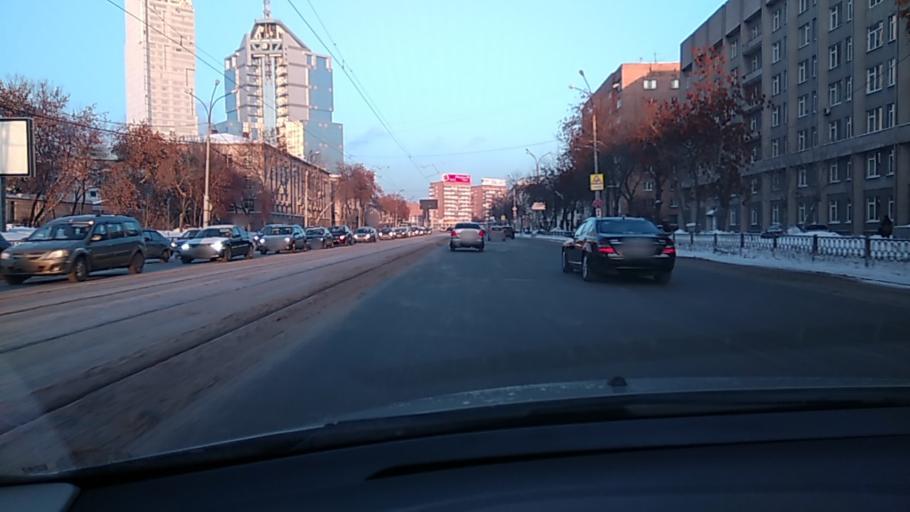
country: RU
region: Sverdlovsk
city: Yekaterinburg
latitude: 56.8531
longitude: 60.5969
